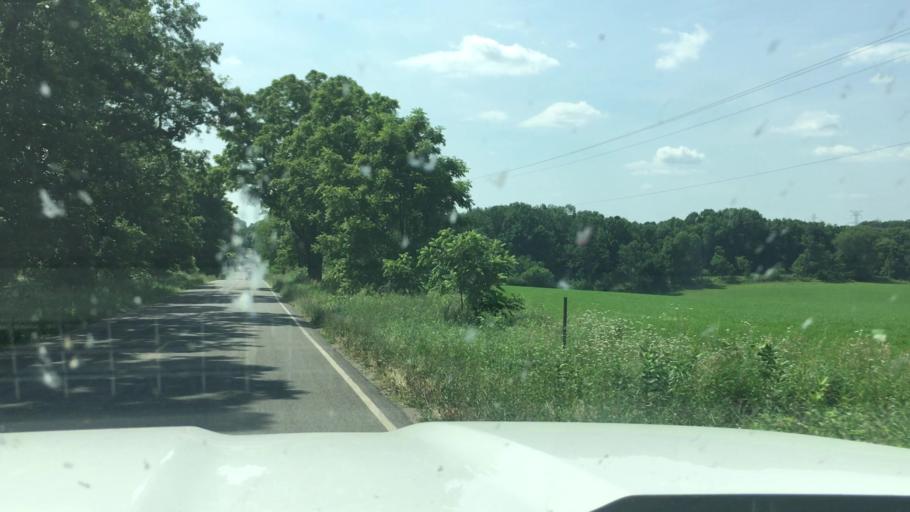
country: US
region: Michigan
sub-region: Kalamazoo County
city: Comstock Northwest
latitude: 42.4287
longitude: -85.5103
